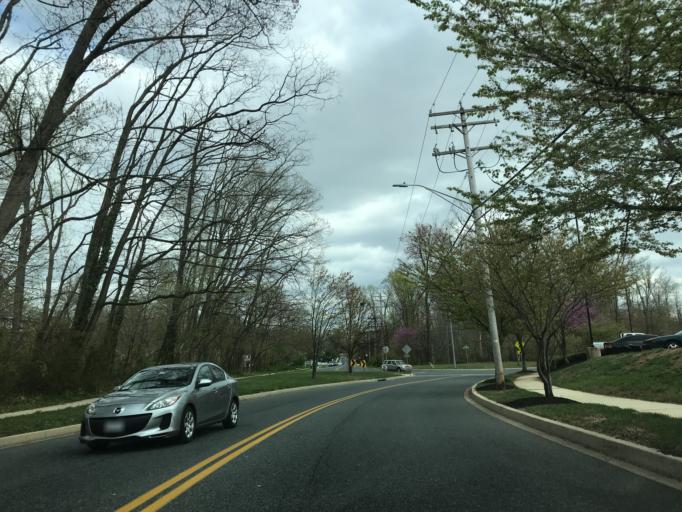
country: US
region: Maryland
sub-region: Harford County
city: Bel Air
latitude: 39.5278
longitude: -76.3491
